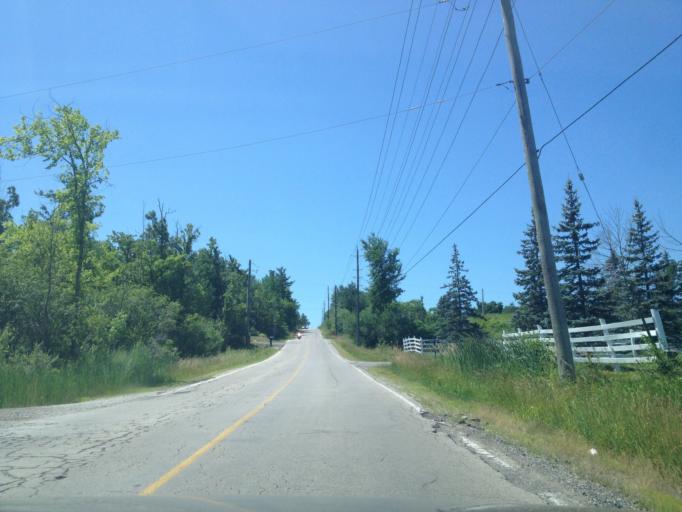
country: CA
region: Ontario
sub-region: Halton
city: Milton
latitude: 43.6608
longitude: -79.9536
